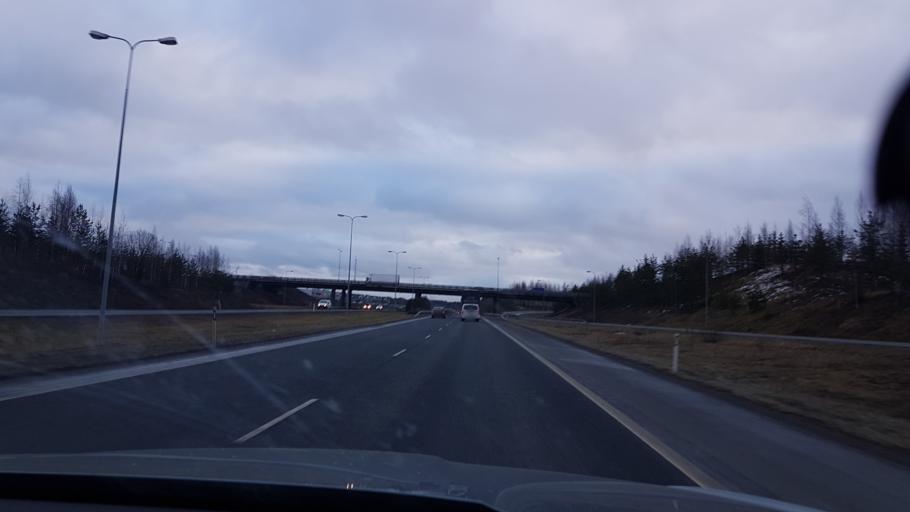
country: FI
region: Pirkanmaa
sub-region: Tampere
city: Lempaeaelae
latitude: 61.3679
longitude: 23.7900
